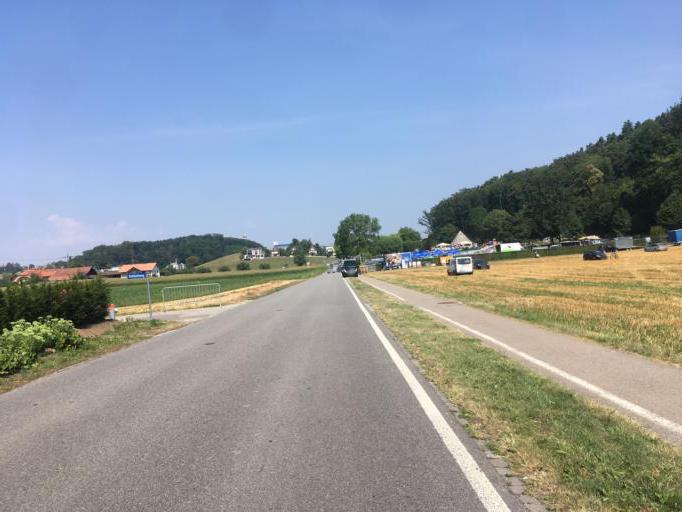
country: CH
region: Bern
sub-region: Bern-Mittelland District
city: Muri
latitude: 46.9441
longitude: 7.4943
